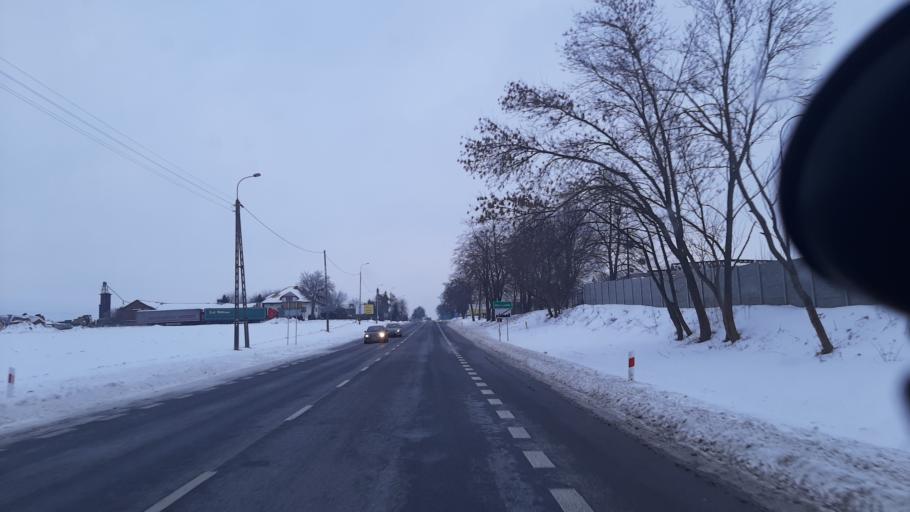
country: PL
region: Lublin Voivodeship
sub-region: Powiat pulawski
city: Markuszow
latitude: 51.3727
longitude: 22.2693
